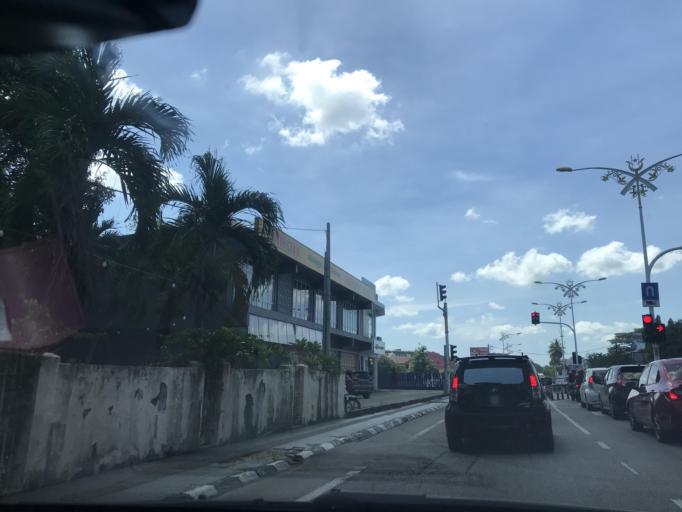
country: MY
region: Kelantan
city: Kota Bharu
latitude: 6.1083
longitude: 102.2527
